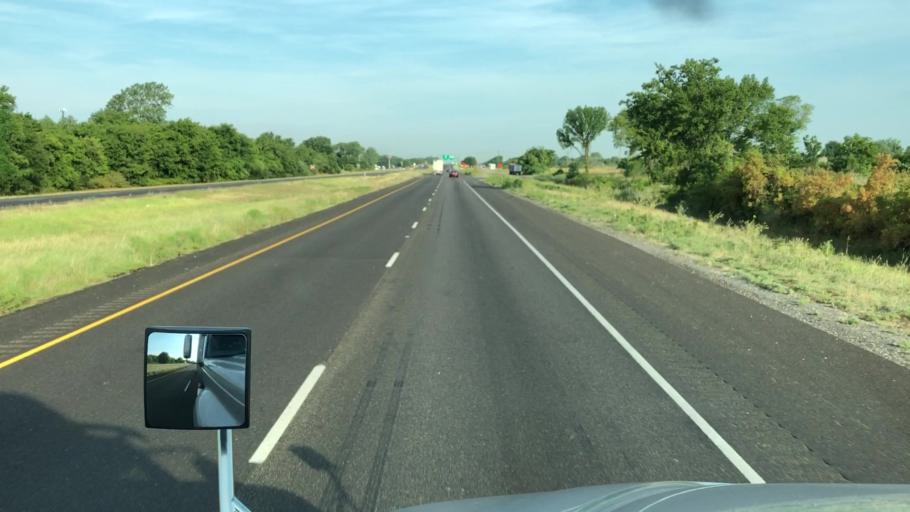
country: US
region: Texas
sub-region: McLennan County
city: Bellmead
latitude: 31.5442
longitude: -97.0587
